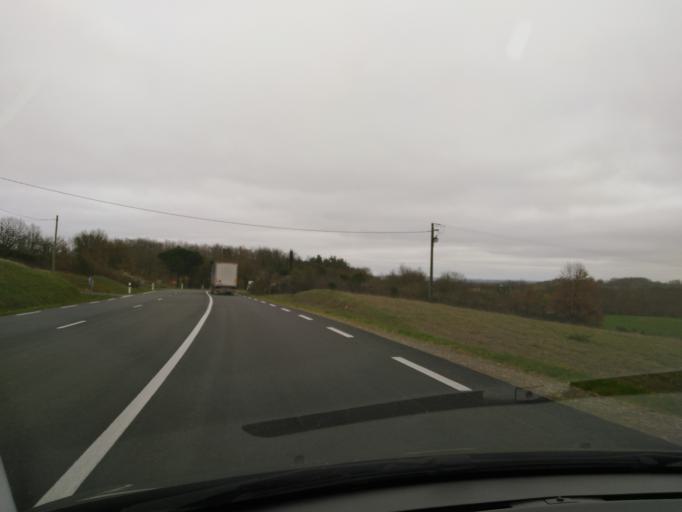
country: FR
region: Aquitaine
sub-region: Departement de la Dordogne
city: Monbazillac
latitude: 44.7315
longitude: 0.5477
